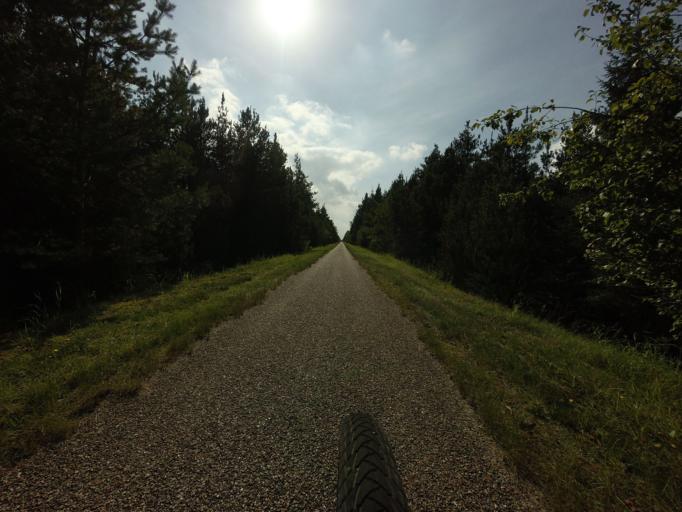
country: DK
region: Central Jutland
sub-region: Viborg Kommune
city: Karup
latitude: 56.2616
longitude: 9.1103
